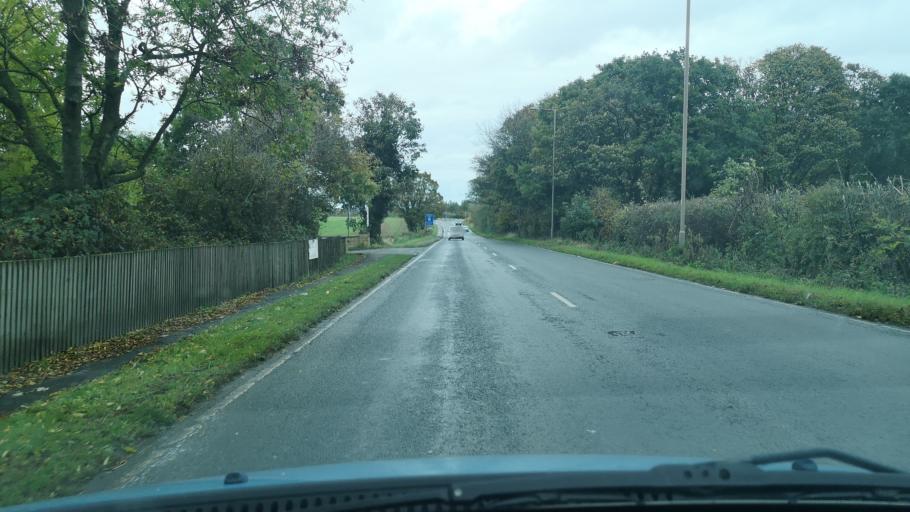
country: GB
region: England
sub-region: City and Borough of Wakefield
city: Hemsworth
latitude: 53.6250
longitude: -1.3412
